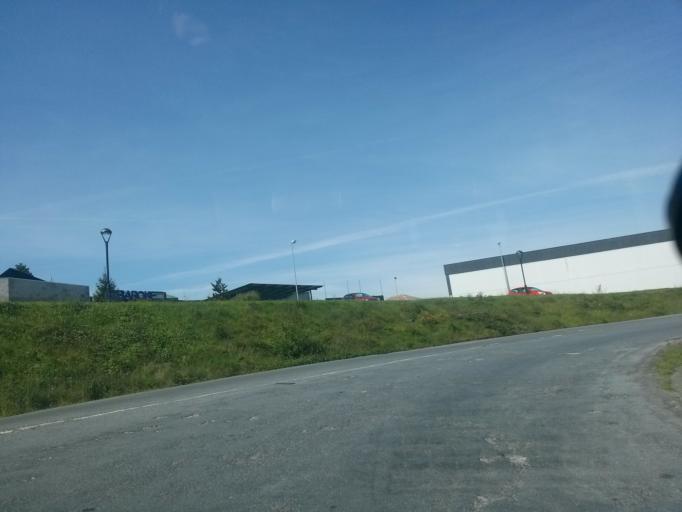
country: ES
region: Galicia
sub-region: Provincia de Lugo
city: Lugo
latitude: 42.9864
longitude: -7.5890
